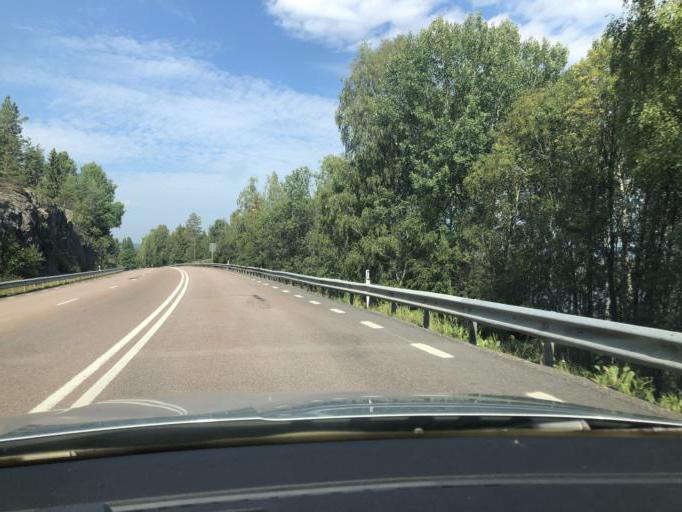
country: SE
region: Vaesternorrland
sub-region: Kramfors Kommun
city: Kramfors
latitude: 62.8121
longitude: 17.8681
